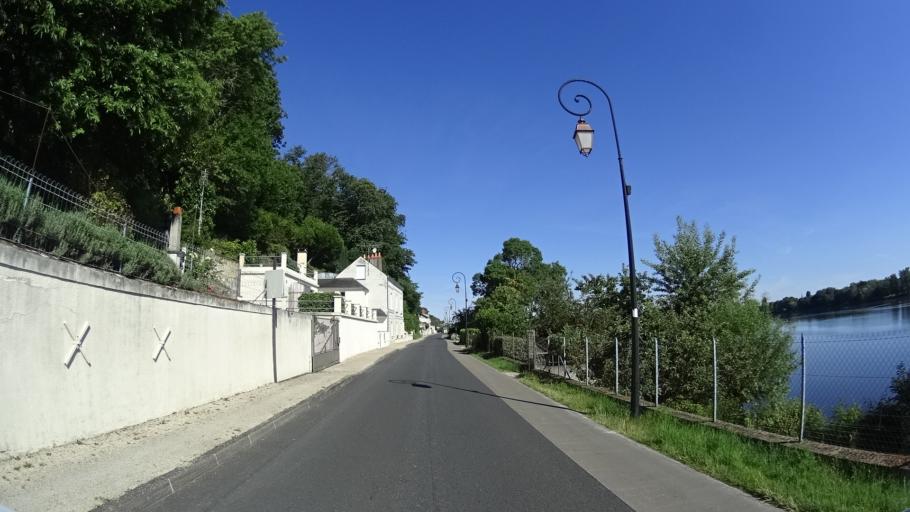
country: FR
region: Pays de la Loire
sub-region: Departement de Maine-et-Loire
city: Saint-Martin-de-la-Place
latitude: 47.3055
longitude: -0.1485
